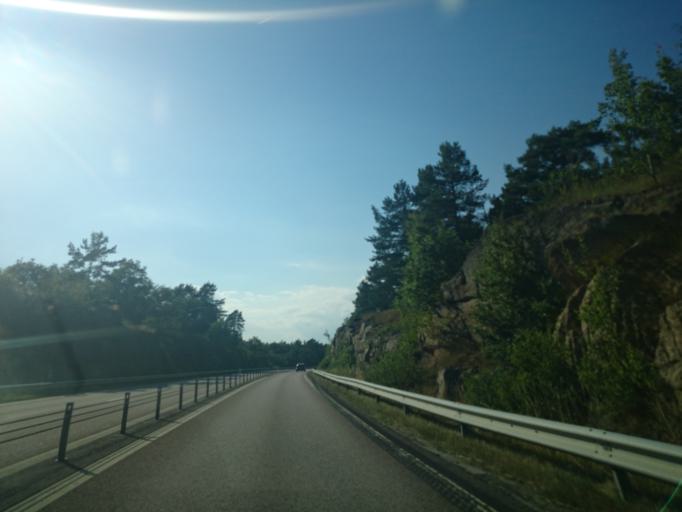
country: SE
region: Blekinge
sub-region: Ronneby Kommun
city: Ronneby
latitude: 56.2161
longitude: 15.2935
